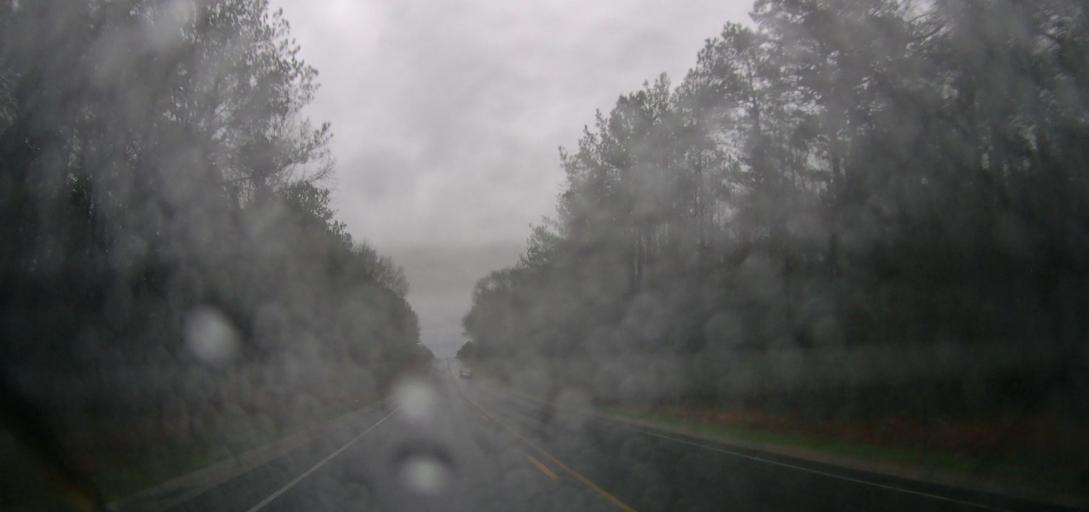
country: US
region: Alabama
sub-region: Autauga County
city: Pine Level
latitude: 32.5912
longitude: -86.7022
